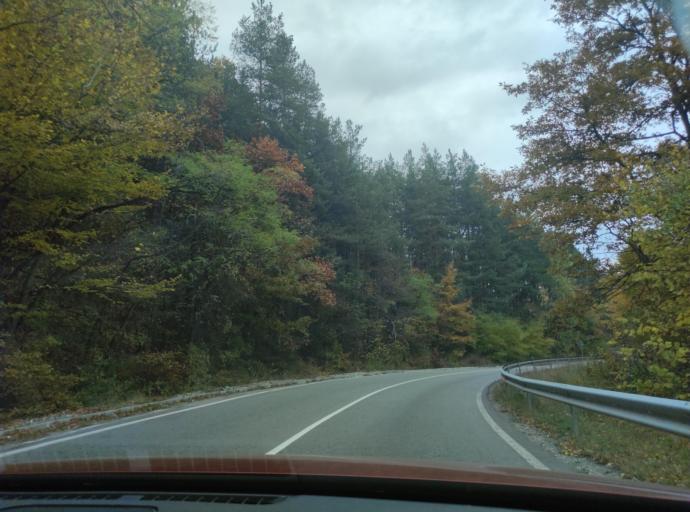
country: BG
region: Sofiya
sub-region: Obshtina Godech
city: Godech
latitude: 42.9776
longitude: 23.1378
